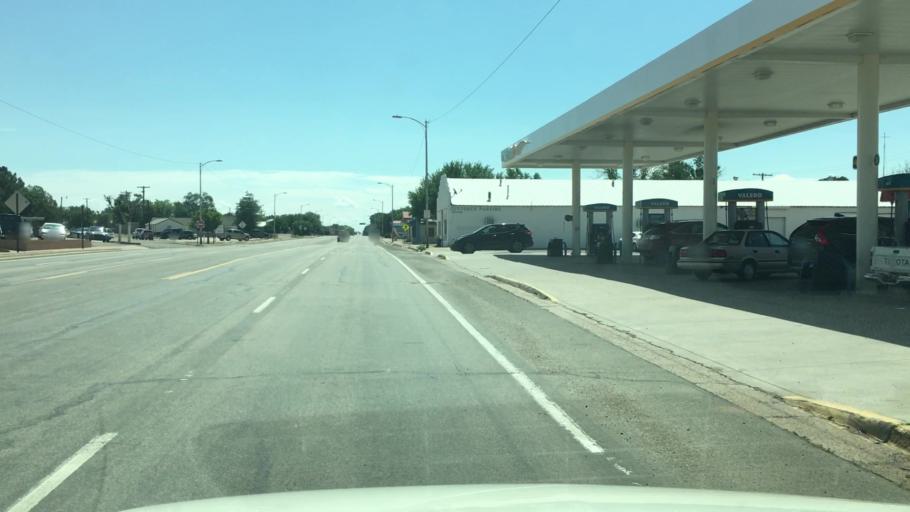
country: US
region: New Mexico
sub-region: De Baca County
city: Fort Sumner
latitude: 34.4709
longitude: -104.2431
